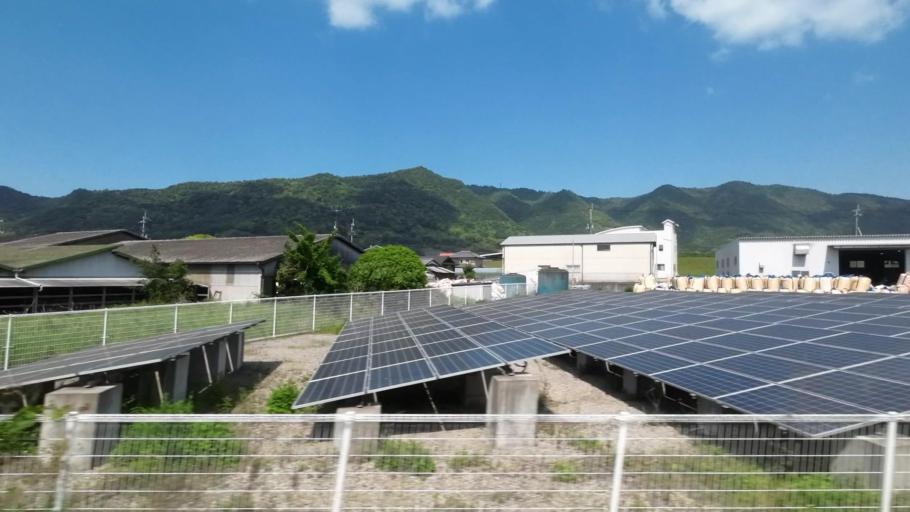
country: JP
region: Kagawa
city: Kan'onjicho
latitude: 34.1584
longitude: 133.6887
